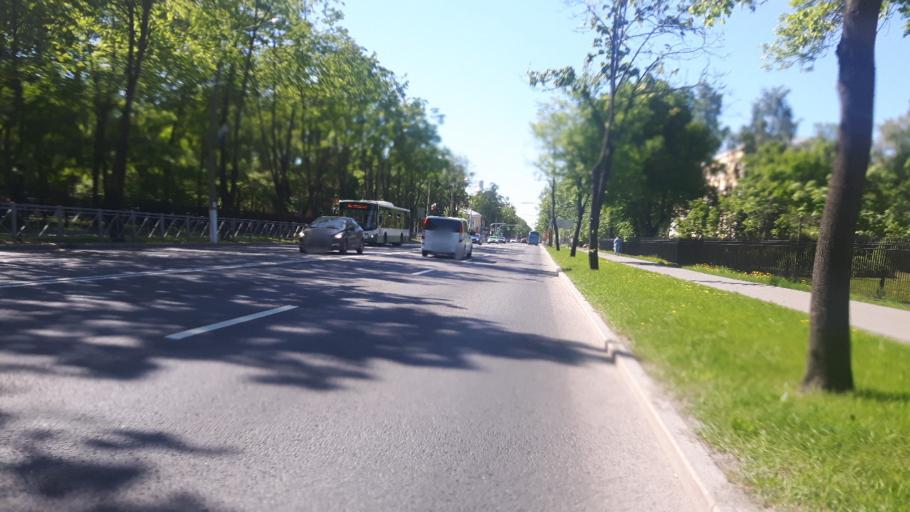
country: RU
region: St.-Petersburg
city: Peterhof
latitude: 59.8774
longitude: 29.9279
